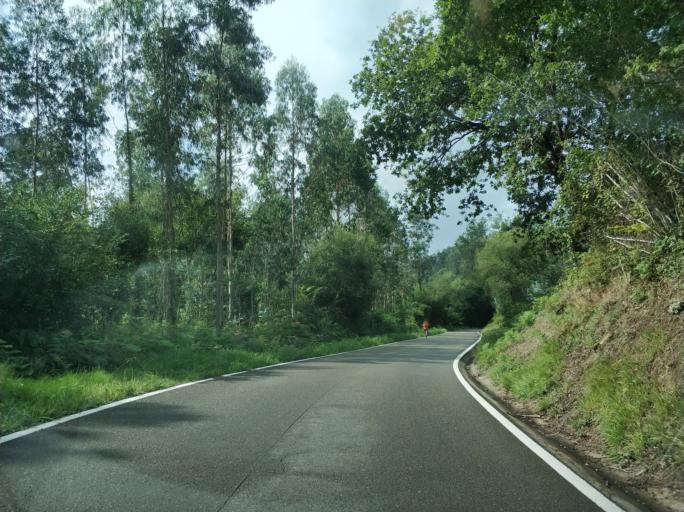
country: ES
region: Cantabria
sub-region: Provincia de Cantabria
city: Polanco
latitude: 43.3879
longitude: -3.9681
